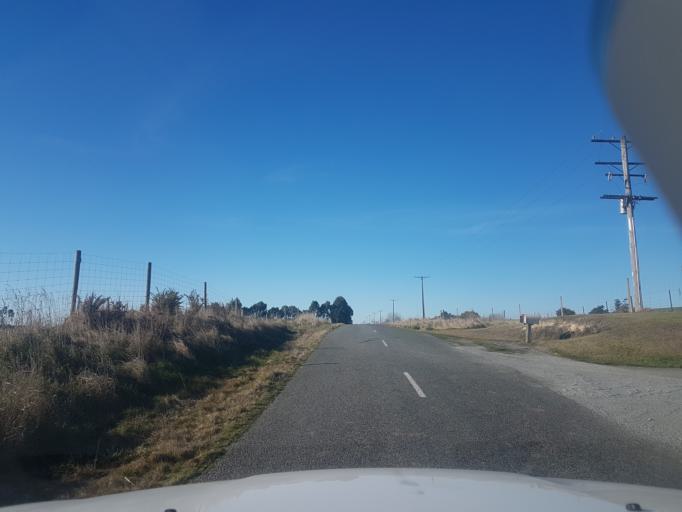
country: NZ
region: Canterbury
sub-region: Timaru District
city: Pleasant Point
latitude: -44.2914
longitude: 171.0602
